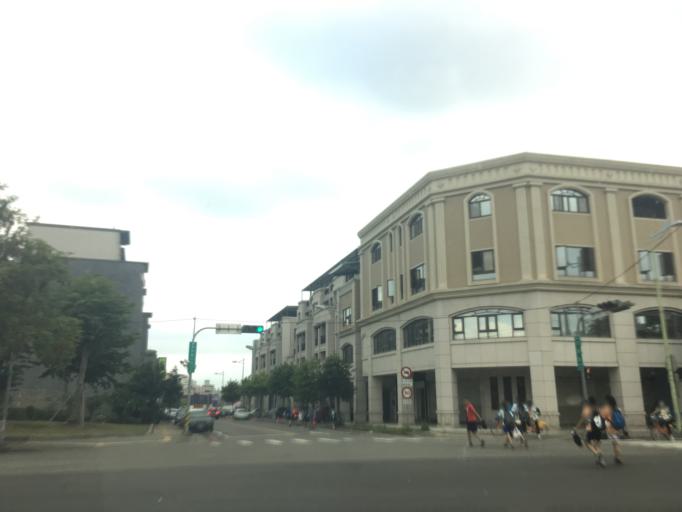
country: TW
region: Taiwan
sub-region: Taichung City
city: Taichung
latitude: 24.1597
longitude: 120.7195
